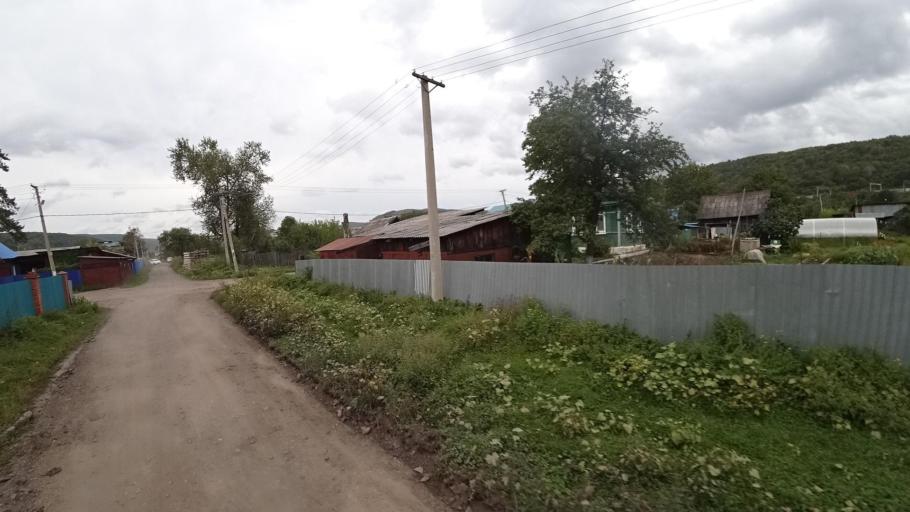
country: RU
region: Jewish Autonomous Oblast
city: Khingansk
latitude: 49.0046
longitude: 131.0521
